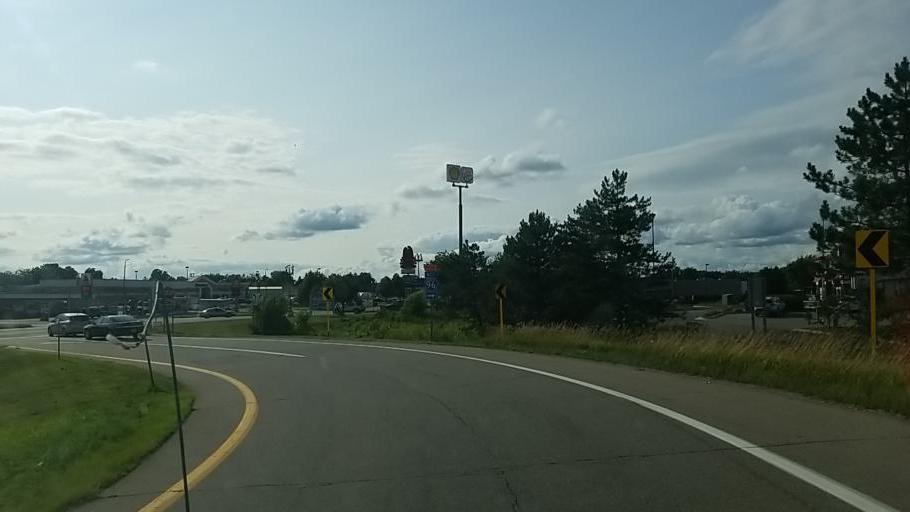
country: US
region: Michigan
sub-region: Ionia County
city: Portland
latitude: 42.8612
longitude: -84.8851
